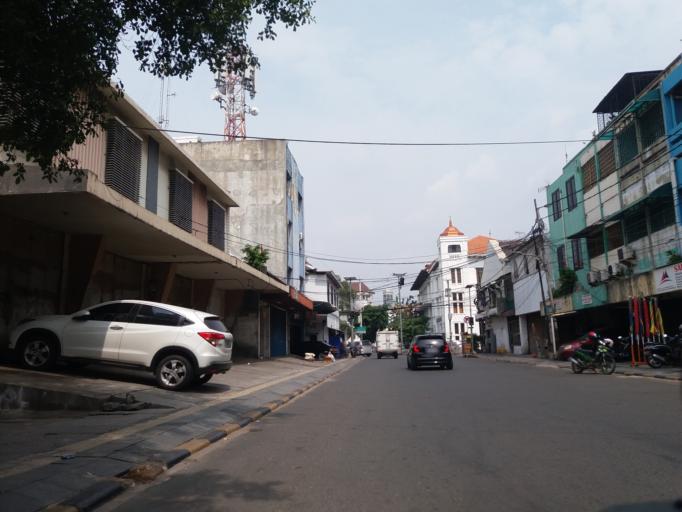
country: ID
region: Jakarta Raya
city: Jakarta
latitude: -6.1331
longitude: 106.8127
